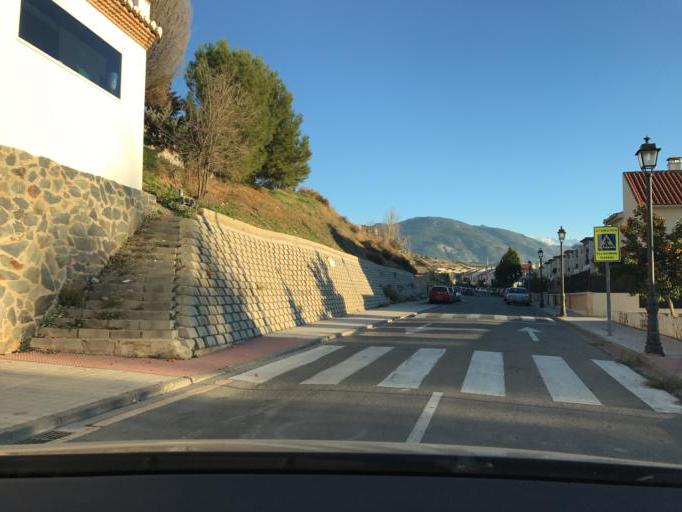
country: ES
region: Andalusia
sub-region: Provincia de Granada
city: Huetor Vega
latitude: 37.1521
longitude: -3.5643
